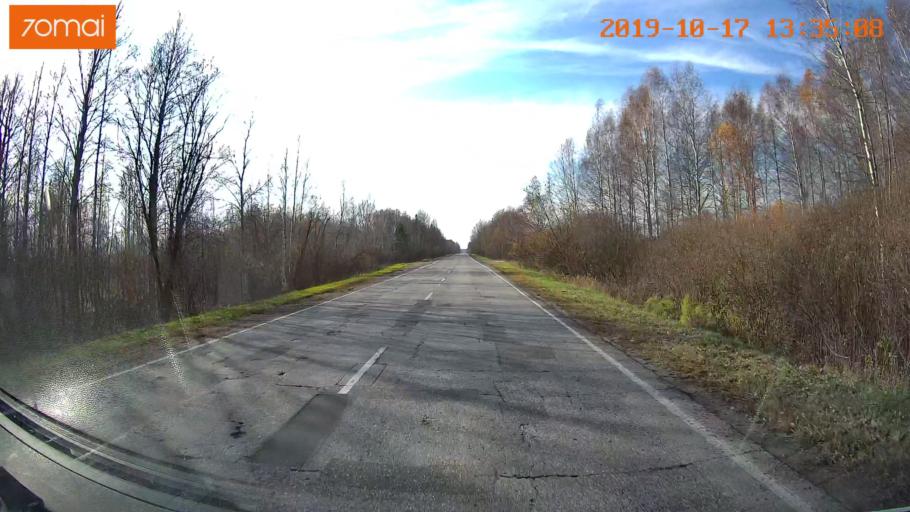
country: RU
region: Vladimir
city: Velikodvorskiy
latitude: 55.1433
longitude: 40.6974
